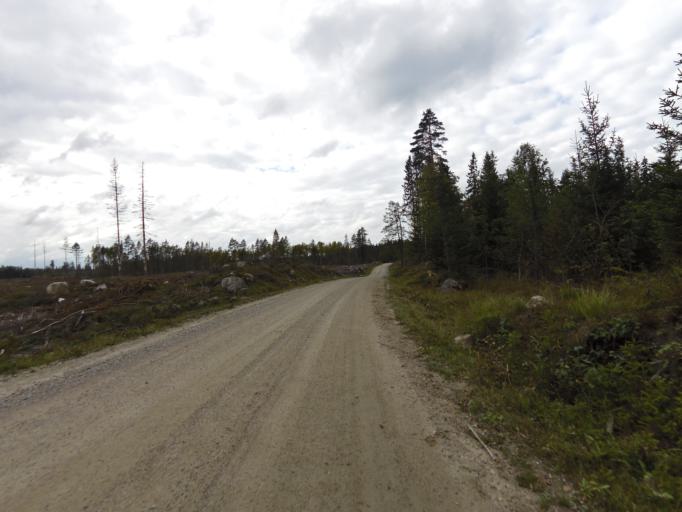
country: SE
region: Gaevleborg
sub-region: Gavle Kommun
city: Valbo
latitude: 60.7659
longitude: 16.9018
